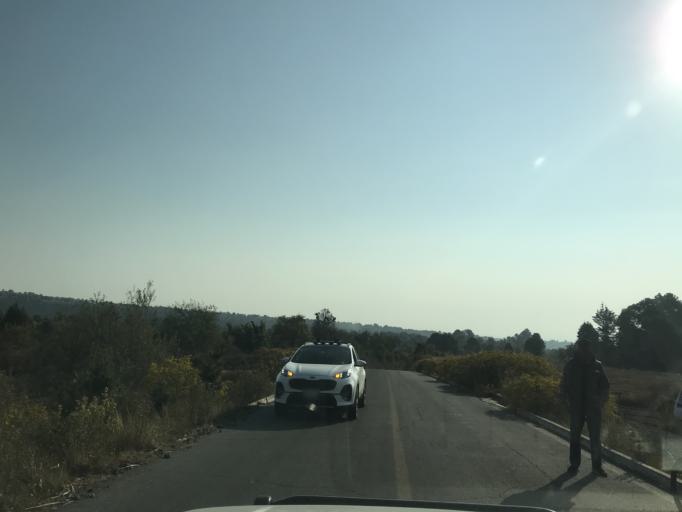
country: MX
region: Puebla
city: San Nicolas de los Ranchos
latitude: 19.0807
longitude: -98.5355
